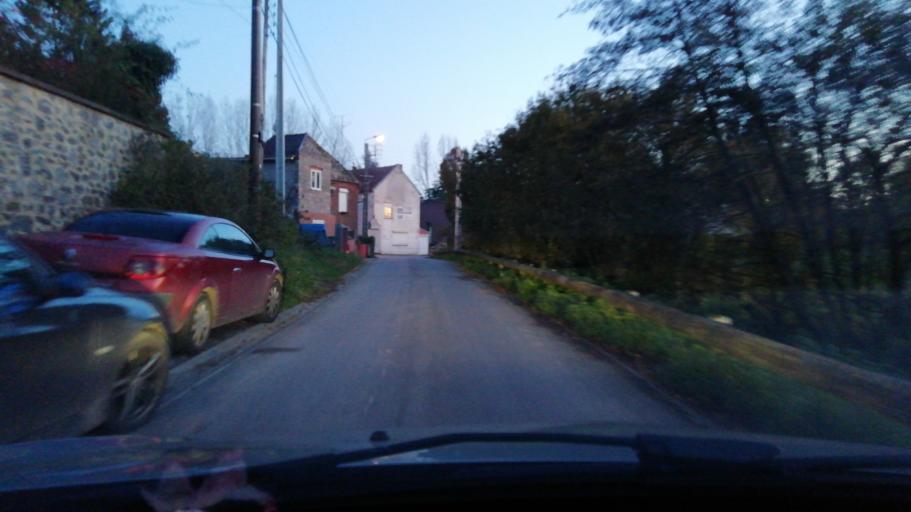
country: FR
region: Nord-Pas-de-Calais
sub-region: Departement du Nord
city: Marpent
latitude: 50.2575
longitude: 4.0786
